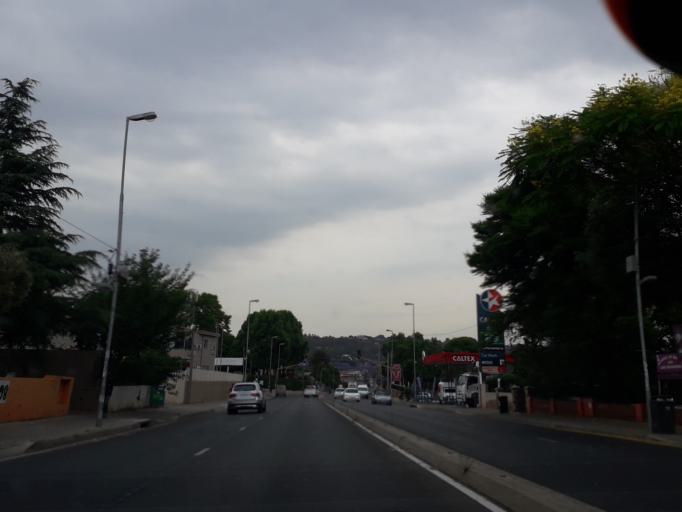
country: ZA
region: Gauteng
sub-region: City of Johannesburg Metropolitan Municipality
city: Johannesburg
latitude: -26.1504
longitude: 28.0865
